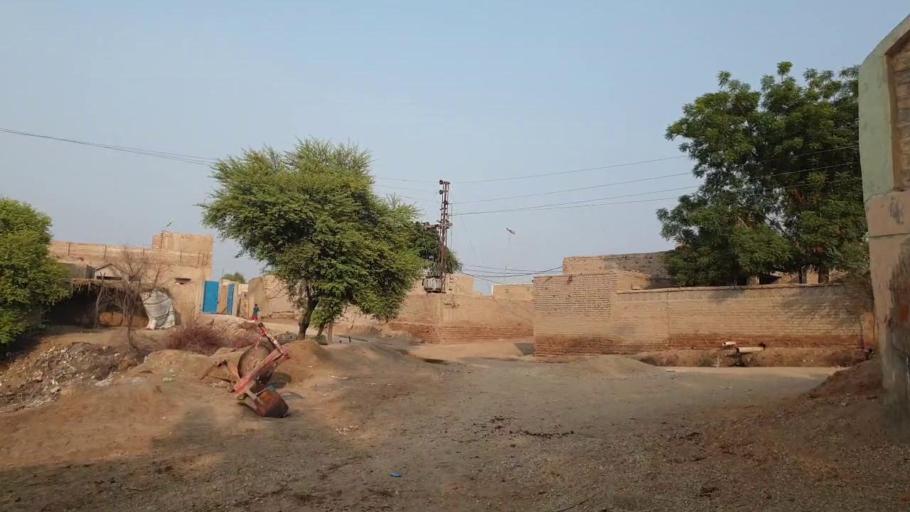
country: PK
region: Sindh
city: Bhan
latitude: 26.4898
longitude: 67.7302
